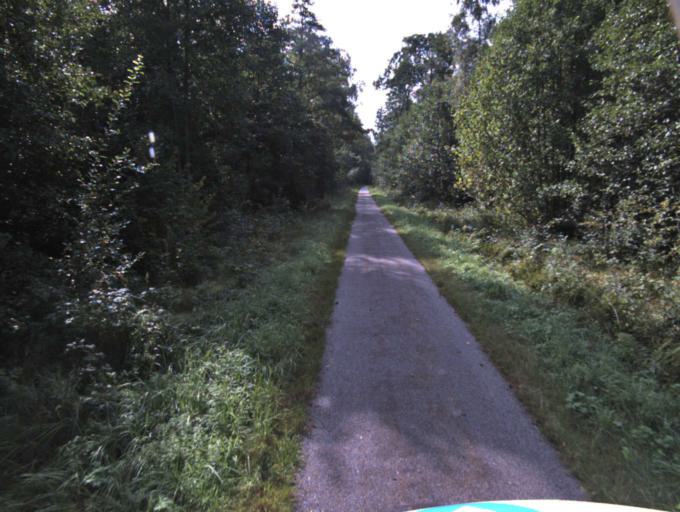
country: SE
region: Vaestra Goetaland
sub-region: Tranemo Kommun
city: Limmared
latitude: 57.6360
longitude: 13.3540
